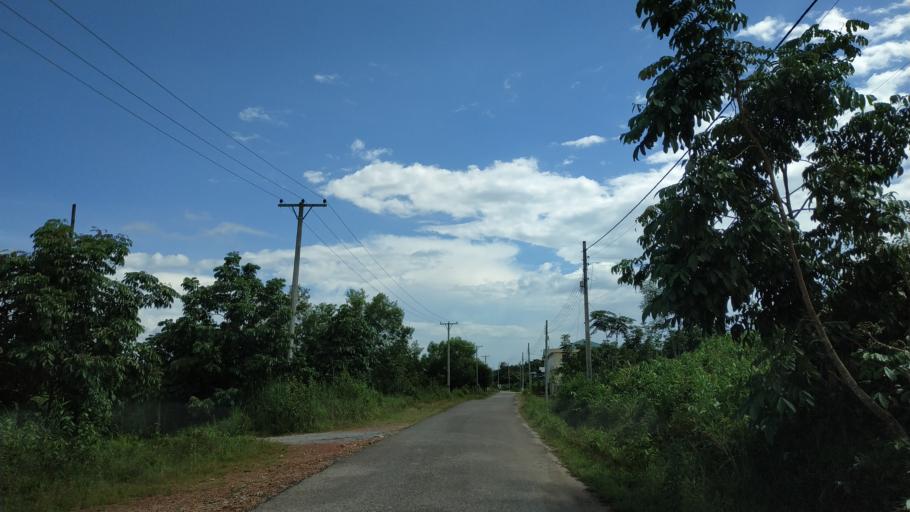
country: MM
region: Tanintharyi
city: Dawei
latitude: 14.2406
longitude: 98.1916
